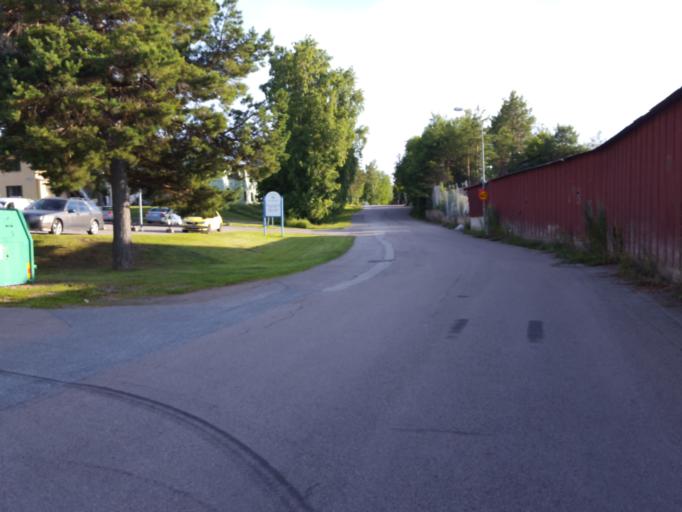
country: SE
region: Uppsala
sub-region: Osthammars Kommun
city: OEsthammar
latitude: 60.2583
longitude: 18.3573
